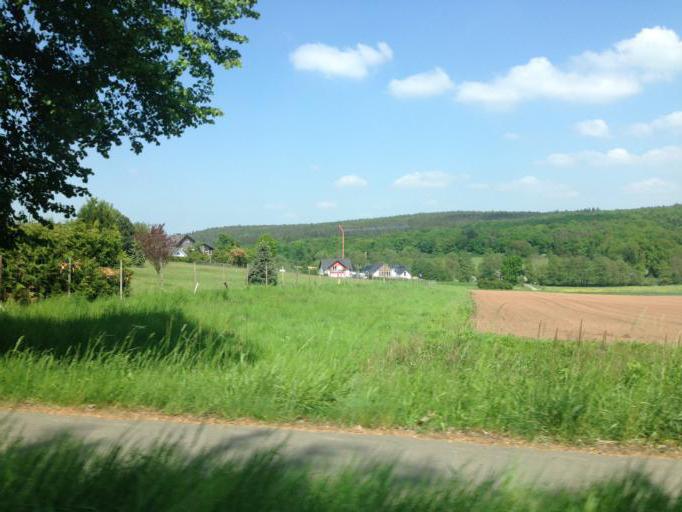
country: DE
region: North Rhine-Westphalia
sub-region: Regierungsbezirk Koln
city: Mechernich
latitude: 50.5866
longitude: 6.6674
